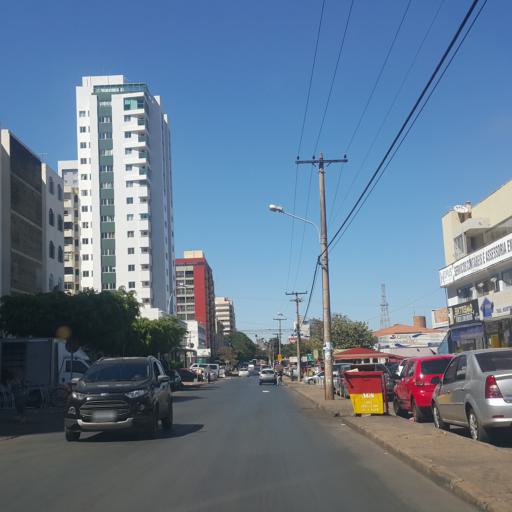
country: BR
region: Federal District
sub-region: Brasilia
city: Brasilia
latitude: -15.8279
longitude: -48.0604
